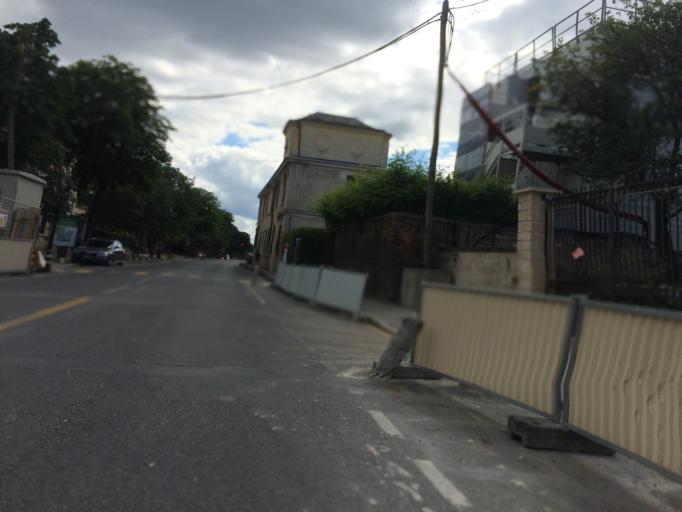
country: FR
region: Ile-de-France
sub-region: Departement des Hauts-de-Seine
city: Neuilly-sur-Seine
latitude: 48.8822
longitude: 2.2593
